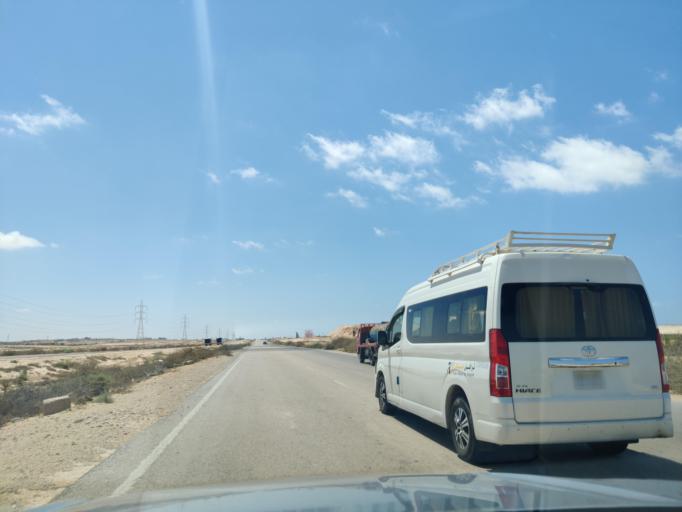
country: EG
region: Muhafazat Matruh
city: Al `Alamayn
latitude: 31.0640
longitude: 28.1937
